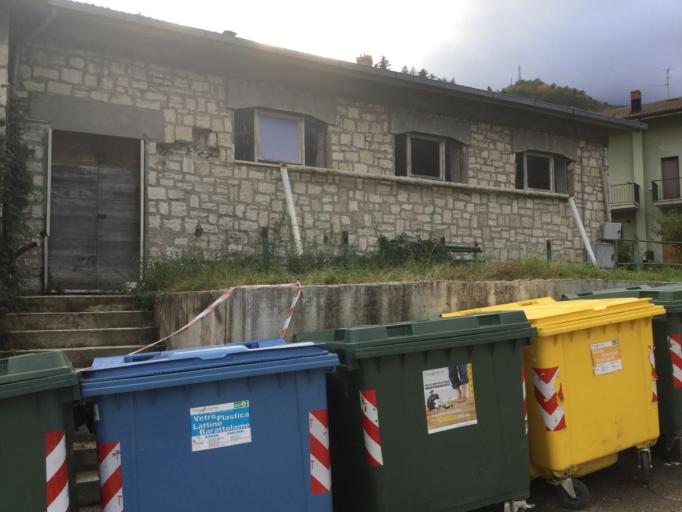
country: IT
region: The Marches
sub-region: Provincia di Ascoli Piceno
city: Arquata del Tronto
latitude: 42.7742
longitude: 13.2985
